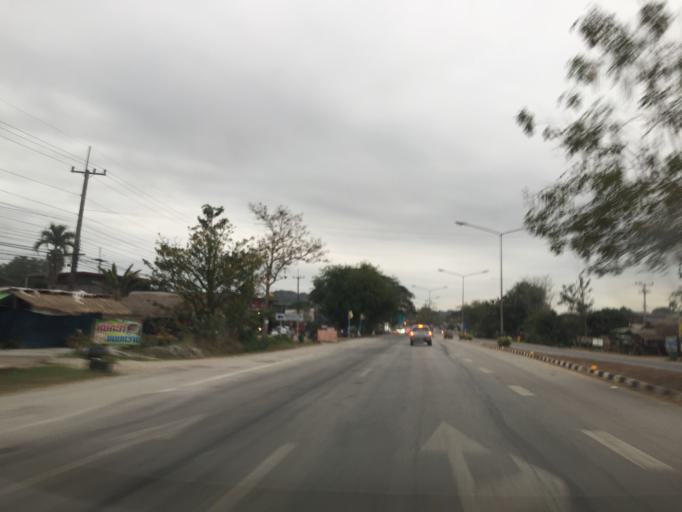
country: TH
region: Loei
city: Erawan
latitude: 17.3041
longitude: 101.9525
